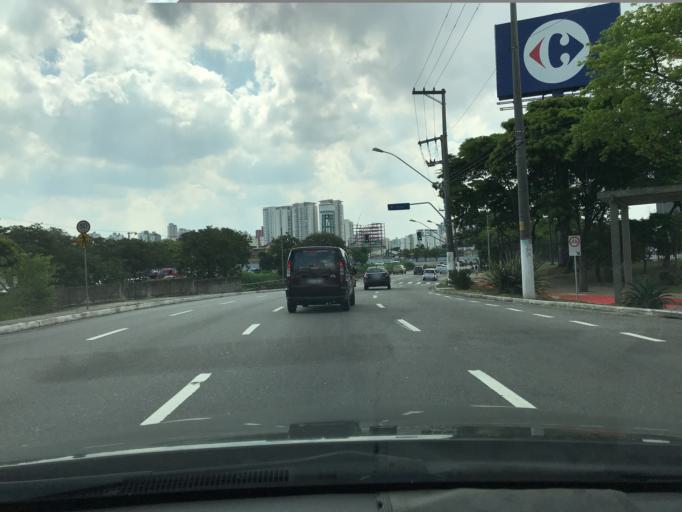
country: BR
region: Sao Paulo
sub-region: Santo Andre
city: Santo Andre
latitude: -23.6485
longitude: -46.5254
